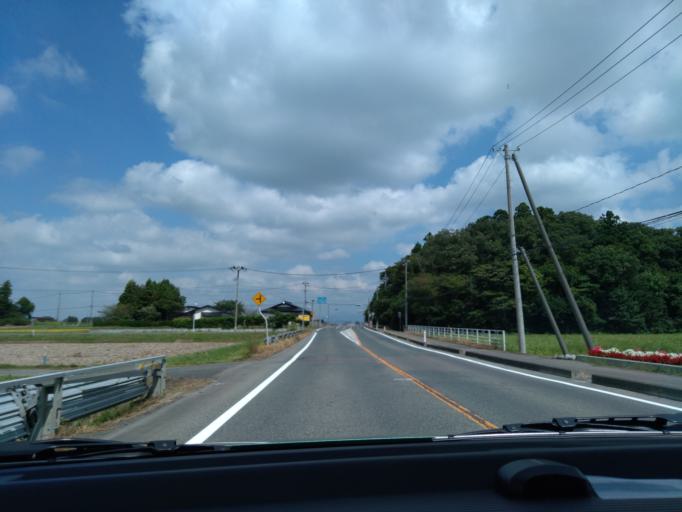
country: JP
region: Iwate
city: Hanamaki
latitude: 39.4337
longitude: 141.0948
